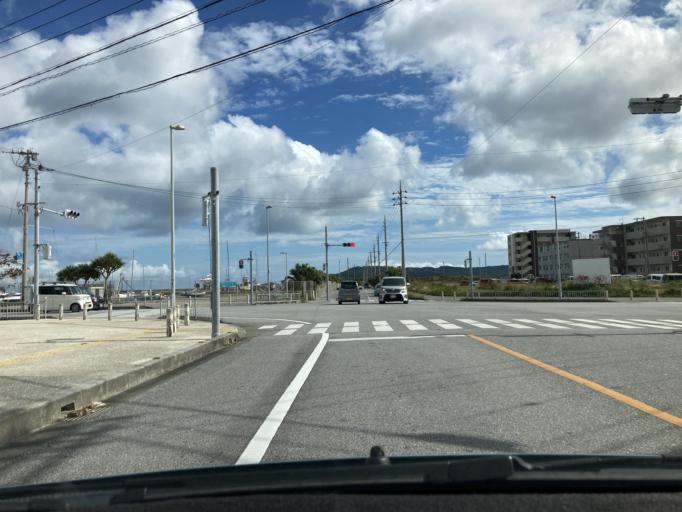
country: JP
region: Okinawa
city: Ginowan
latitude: 26.2048
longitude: 127.7641
